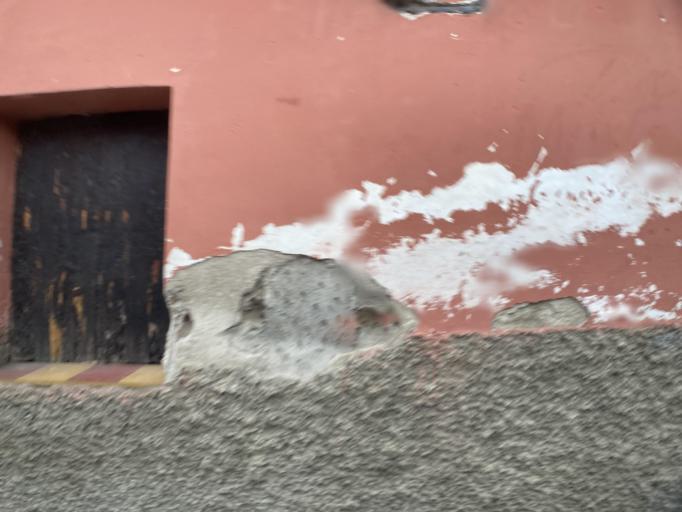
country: GT
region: Sacatepequez
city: Jocotenango
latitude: 14.5747
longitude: -90.7401
